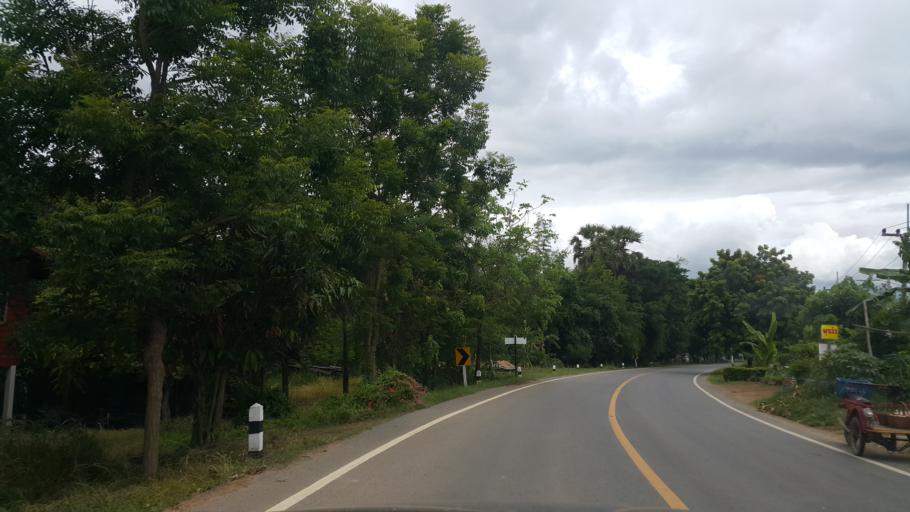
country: TH
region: Sukhothai
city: Ban Na
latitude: 17.0381
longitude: 99.7040
